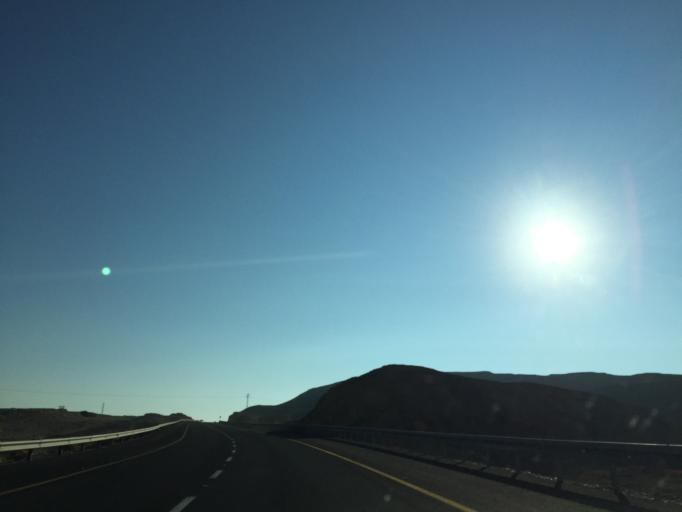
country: IL
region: Southern District
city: Mitzpe Ramon
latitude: 30.2998
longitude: 34.9686
